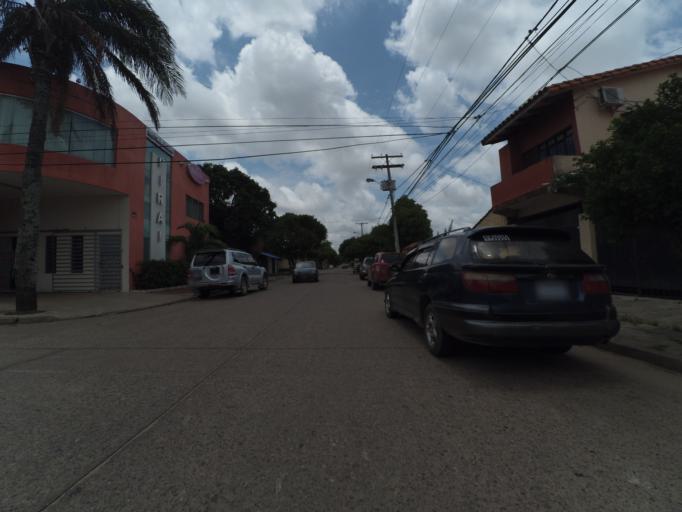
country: BO
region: Santa Cruz
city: Santa Cruz de la Sierra
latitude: -17.7887
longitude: -63.1971
